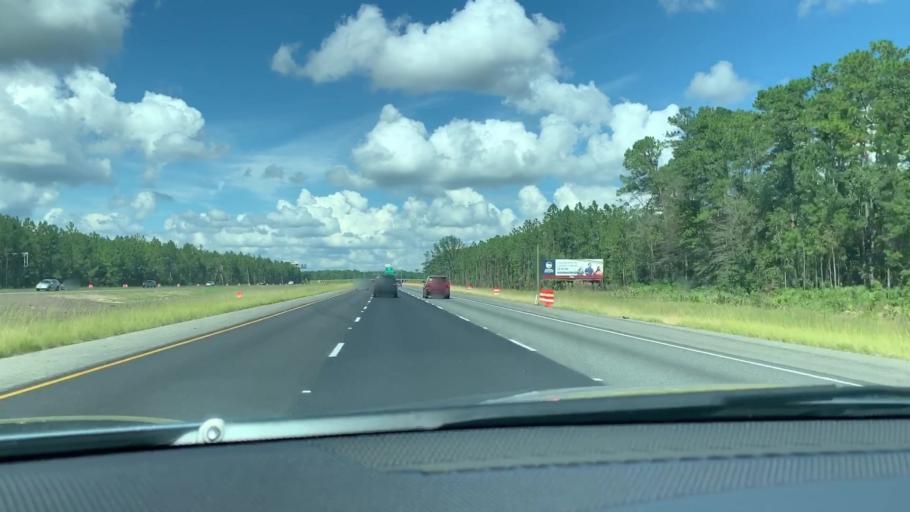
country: US
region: Georgia
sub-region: Camden County
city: Woodbine
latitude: 30.9351
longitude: -81.6859
